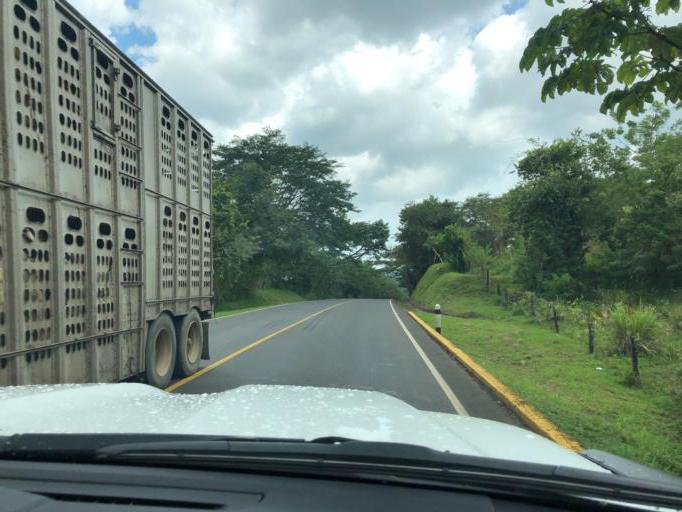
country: NI
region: Chontales
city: Villa Sandino
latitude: 11.9976
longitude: -84.8787
